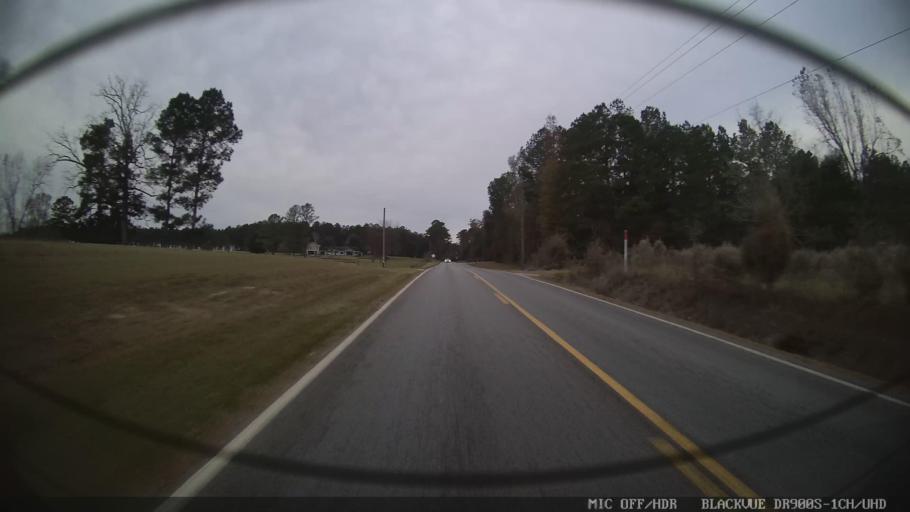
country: US
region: Mississippi
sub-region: Clarke County
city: Quitman
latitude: 32.0288
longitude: -88.8127
